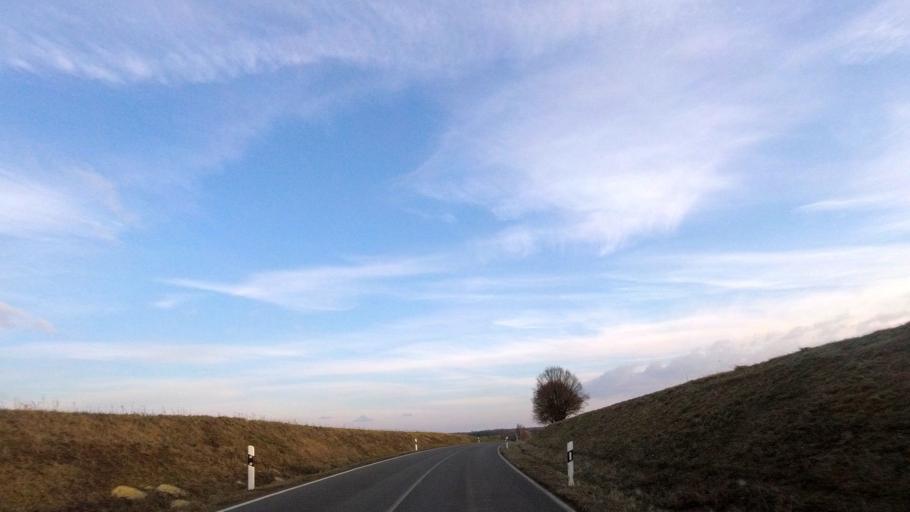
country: DE
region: Brandenburg
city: Niemegk
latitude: 52.0843
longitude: 12.6414
